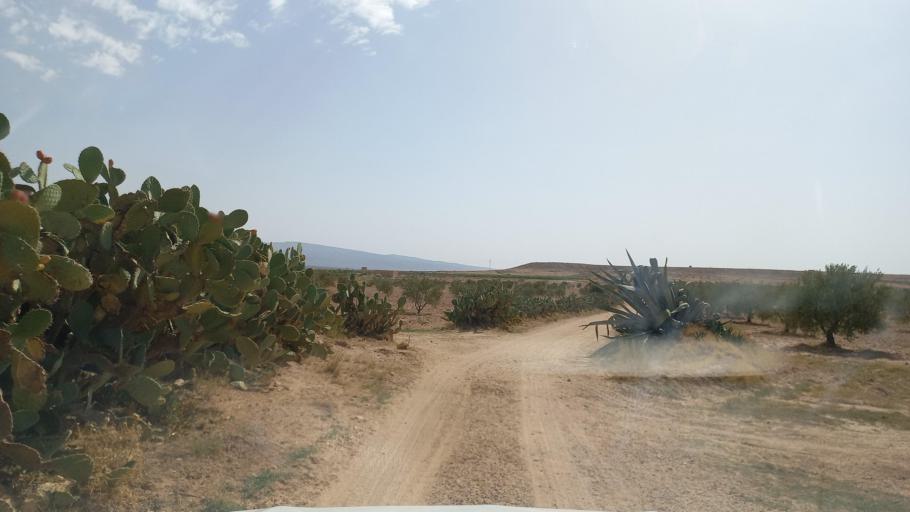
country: TN
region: Al Qasrayn
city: Kasserine
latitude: 35.2759
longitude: 8.9693
